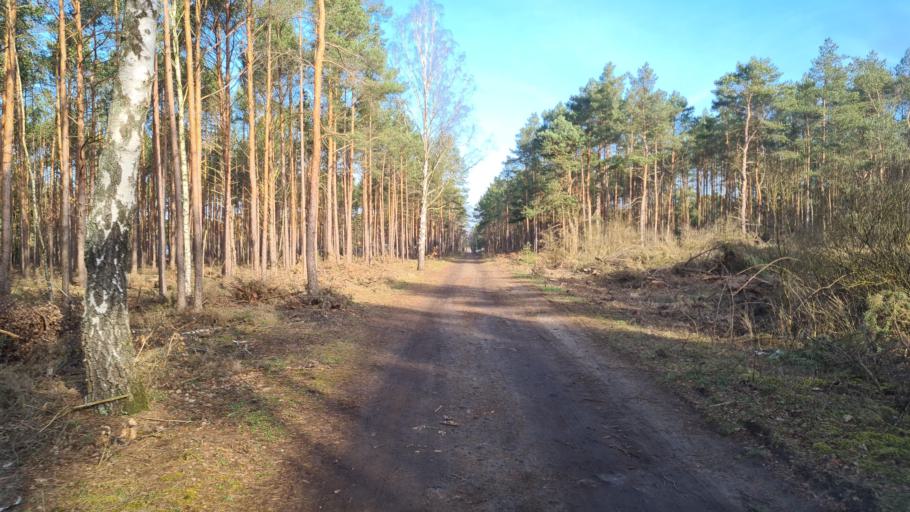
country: DE
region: Brandenburg
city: Gross Koris
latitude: 52.1576
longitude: 13.6929
